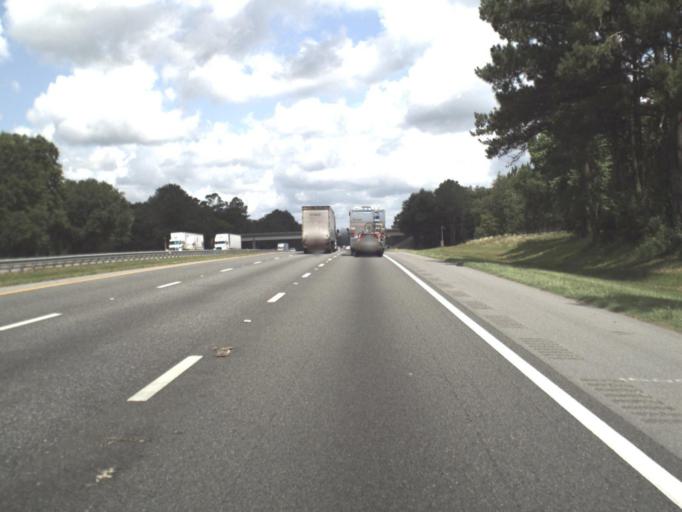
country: US
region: Florida
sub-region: Suwannee County
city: Wellborn
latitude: 30.2889
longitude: -82.7742
